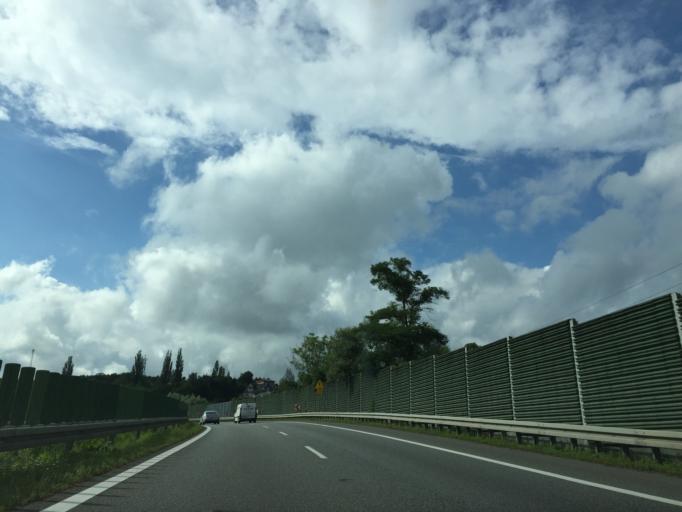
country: PL
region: Lesser Poland Voivodeship
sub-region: Powiat myslenicki
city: Myslenice
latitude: 49.8402
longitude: 19.9460
